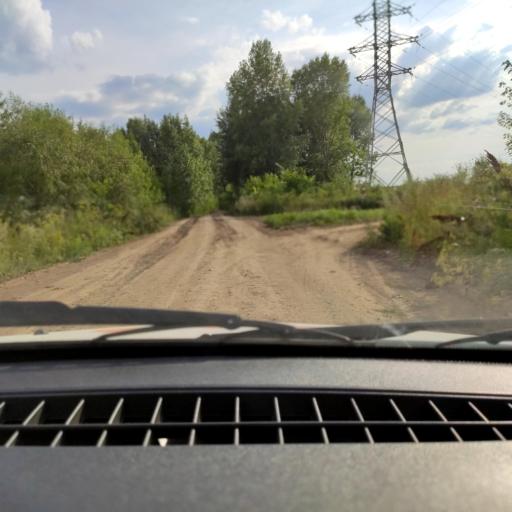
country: RU
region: Bashkortostan
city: Mikhaylovka
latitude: 54.9192
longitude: 55.9324
